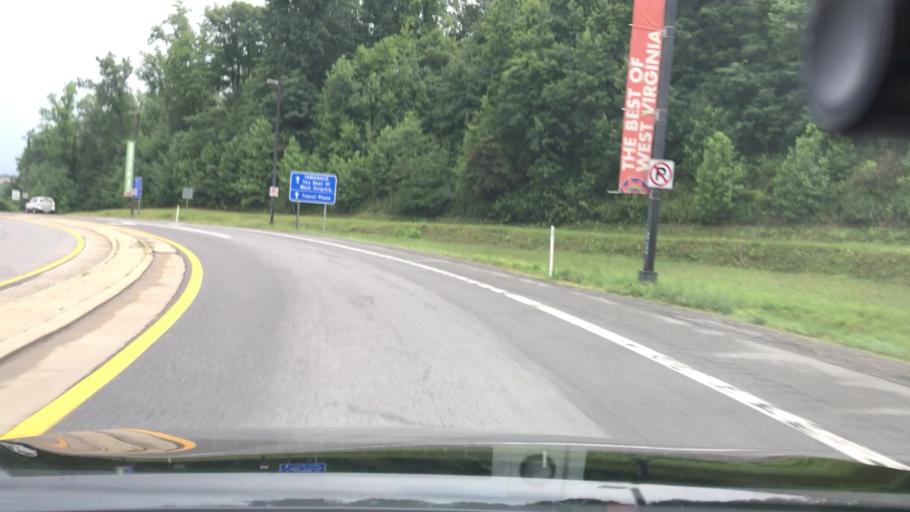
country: US
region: West Virginia
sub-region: Raleigh County
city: Prosperity
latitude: 37.8107
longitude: -81.2147
